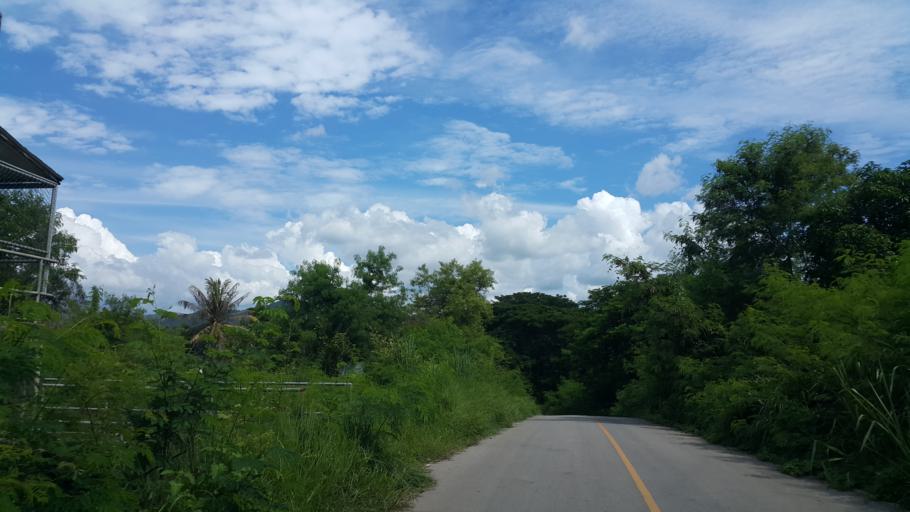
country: TH
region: Chiang Mai
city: Mae On
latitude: 18.7399
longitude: 99.2019
